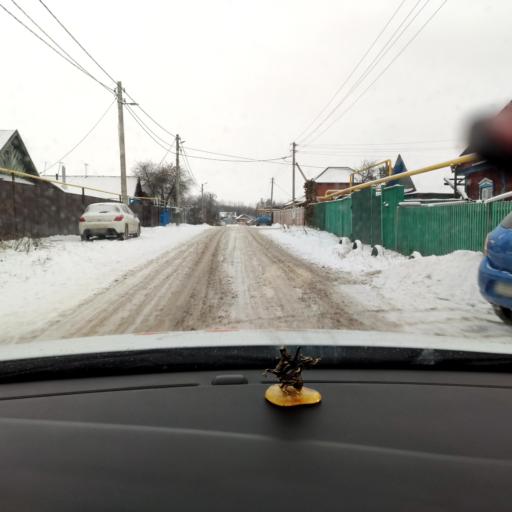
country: RU
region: Tatarstan
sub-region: Gorod Kazan'
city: Kazan
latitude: 55.7383
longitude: 49.0997
